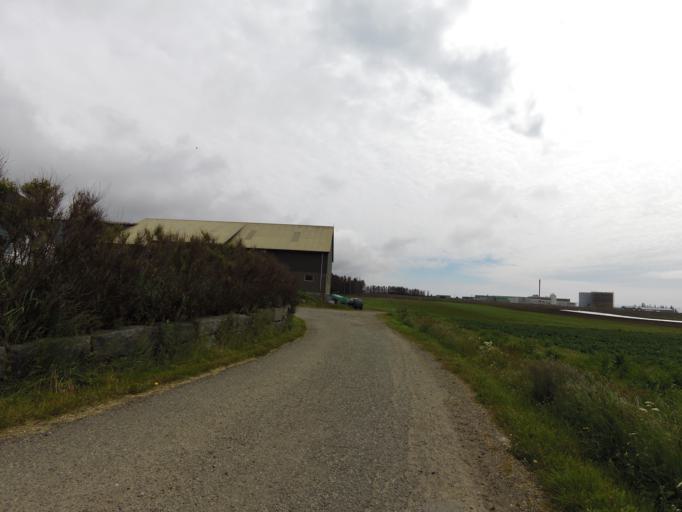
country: NO
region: Rogaland
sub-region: Ha
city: Naerbo
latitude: 58.6352
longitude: 5.5989
